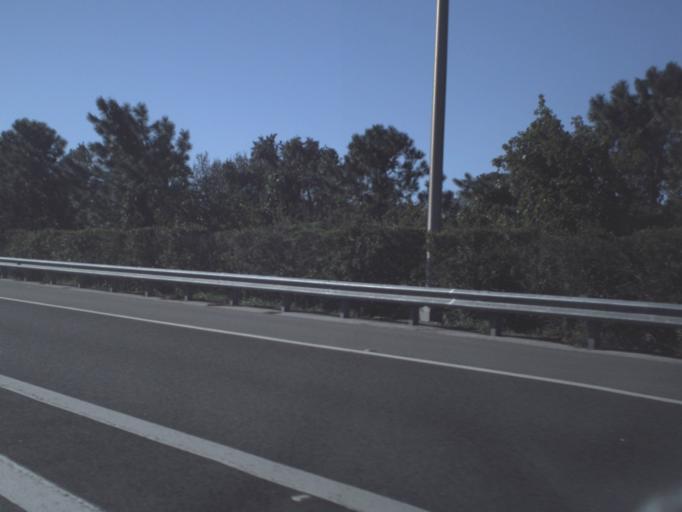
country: US
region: Florida
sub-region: Seminole County
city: Lake Mary
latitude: 28.7819
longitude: -81.3005
